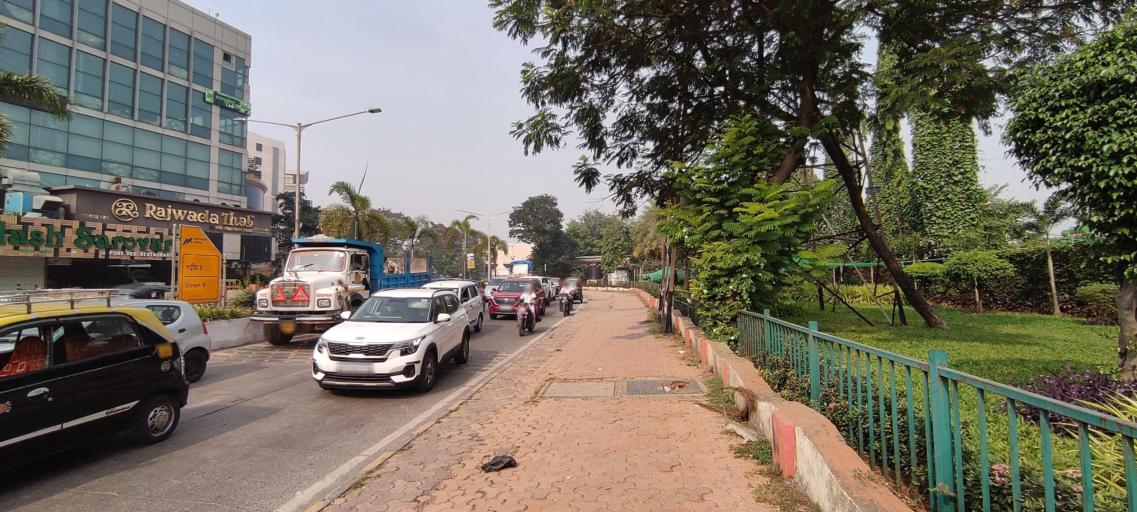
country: IN
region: Maharashtra
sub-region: Mumbai Suburban
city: Mumbai
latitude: 19.0655
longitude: 72.8620
